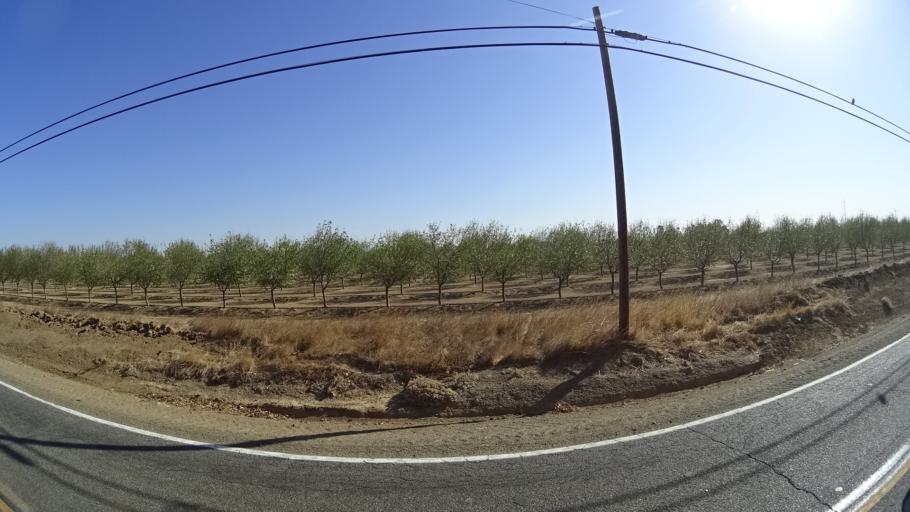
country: US
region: California
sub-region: Yolo County
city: Woodland
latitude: 38.6651
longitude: -121.8581
